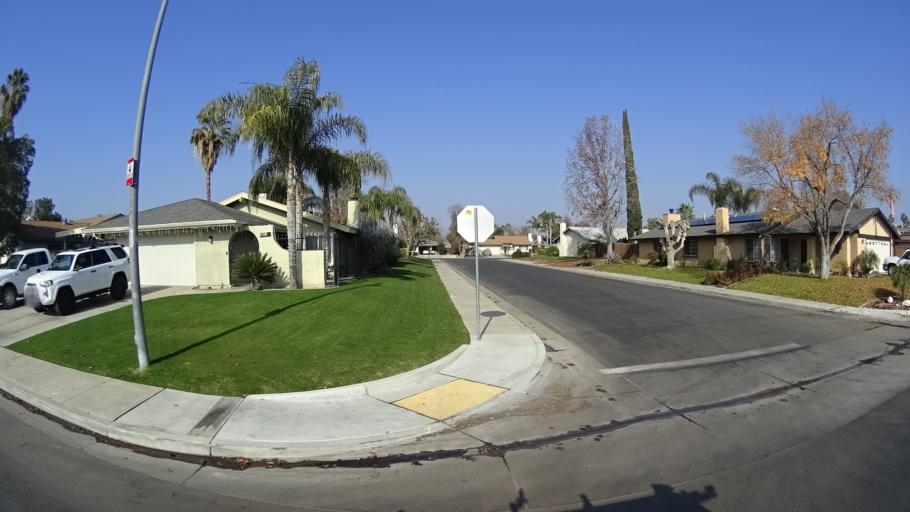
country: US
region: California
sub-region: Kern County
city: Greenacres
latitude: 35.3219
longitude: -119.0718
